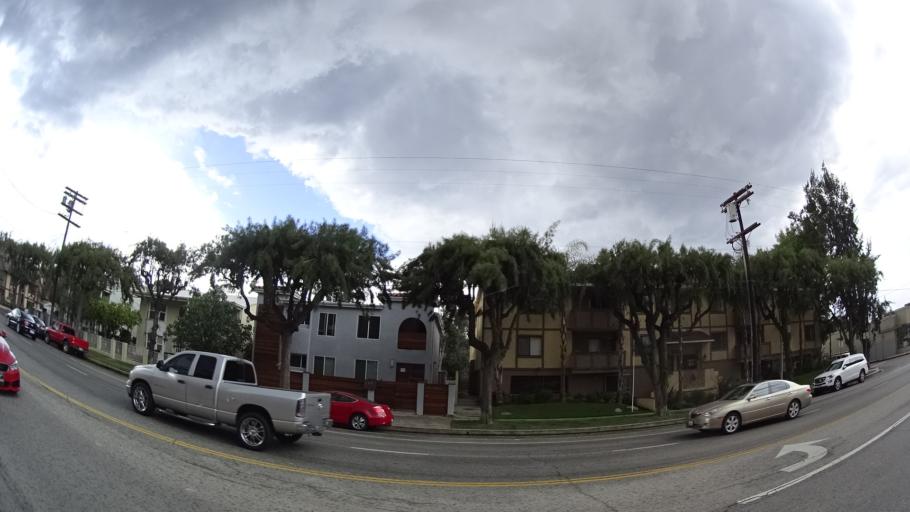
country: US
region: California
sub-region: Los Angeles County
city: Sherman Oaks
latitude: 34.1577
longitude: -118.4204
